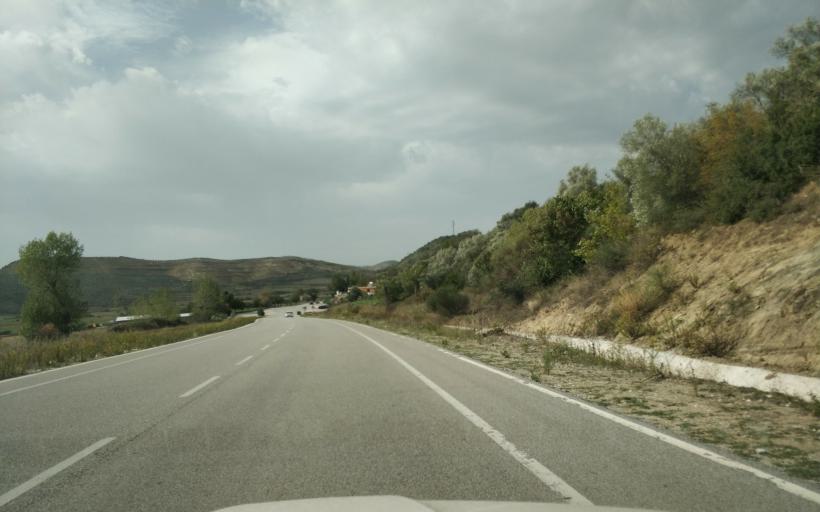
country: AL
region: Gjirokaster
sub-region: Rrethi i Tepelenes
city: Krahes
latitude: 40.3869
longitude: 19.8839
